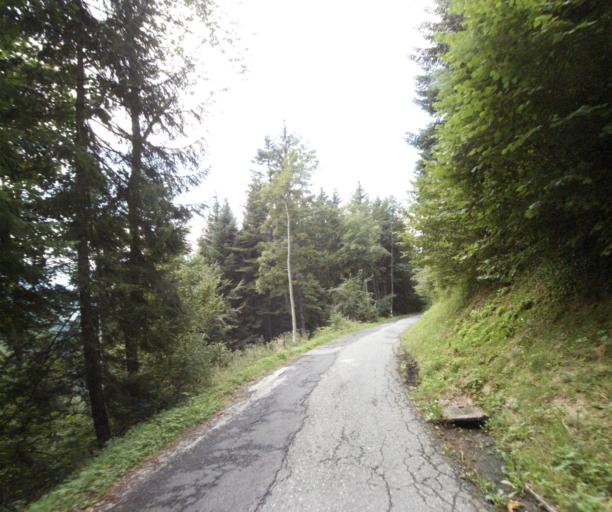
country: CH
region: Vaud
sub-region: Riviera-Pays-d'Enhaut District
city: Caux
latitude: 46.4122
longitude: 6.9552
